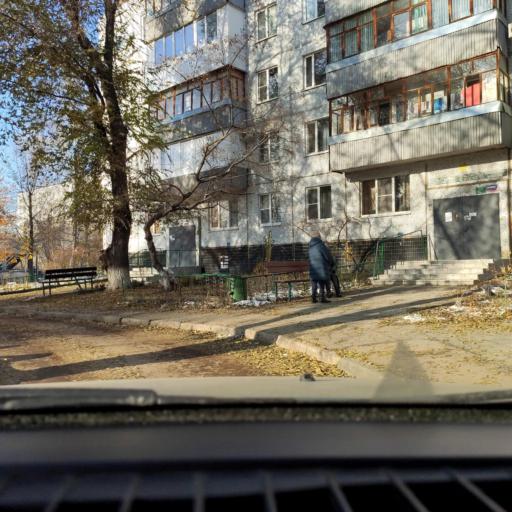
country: RU
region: Samara
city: Tol'yatti
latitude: 53.5126
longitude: 49.2890
